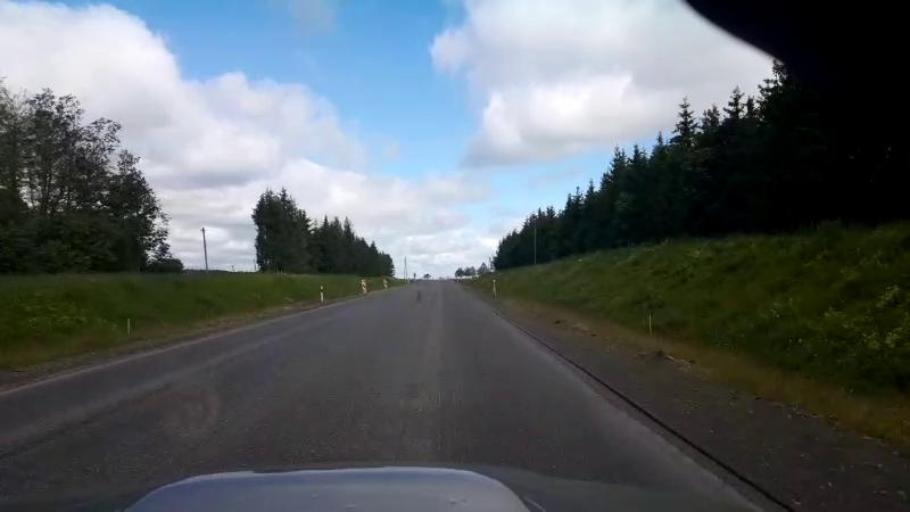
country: LV
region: Bauskas Rajons
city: Bauska
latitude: 56.3292
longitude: 24.3037
